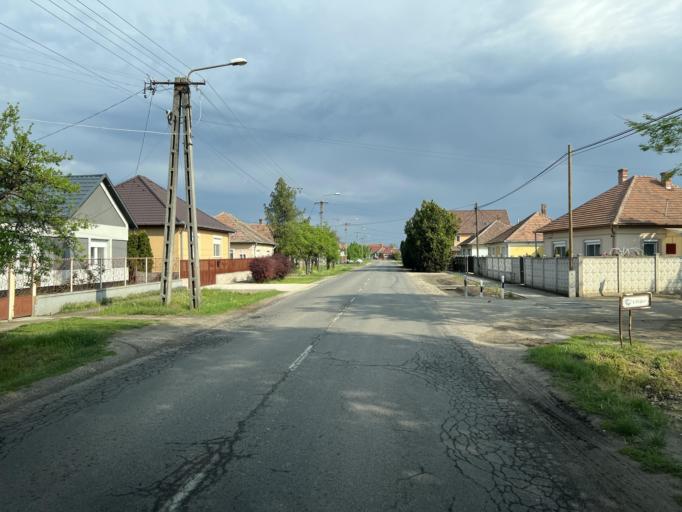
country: HU
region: Pest
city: Tapioszentmarton
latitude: 47.3335
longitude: 19.7540
